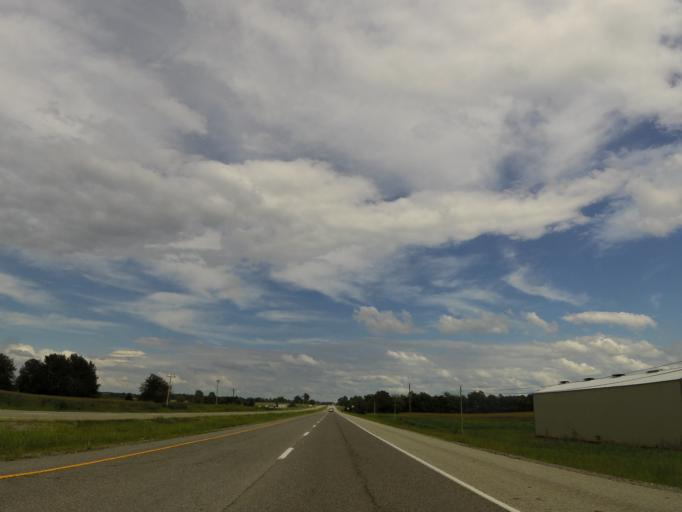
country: US
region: Kentucky
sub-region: Trigg County
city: Cadiz
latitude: 36.8829
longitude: -87.7008
